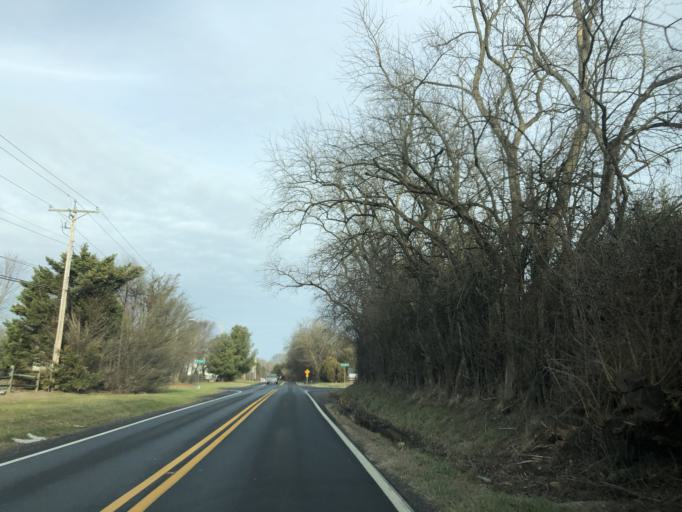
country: US
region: Delaware
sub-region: New Castle County
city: Townsend
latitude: 39.4450
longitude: -75.6460
